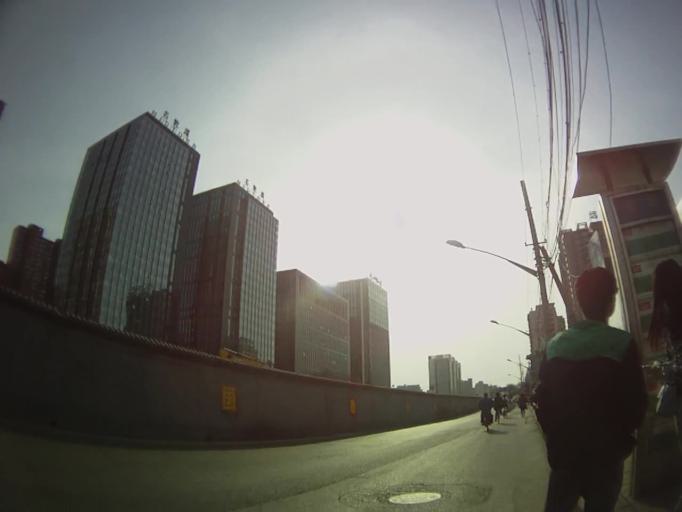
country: CN
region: Beijing
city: Longtan
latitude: 39.8926
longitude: 116.4421
